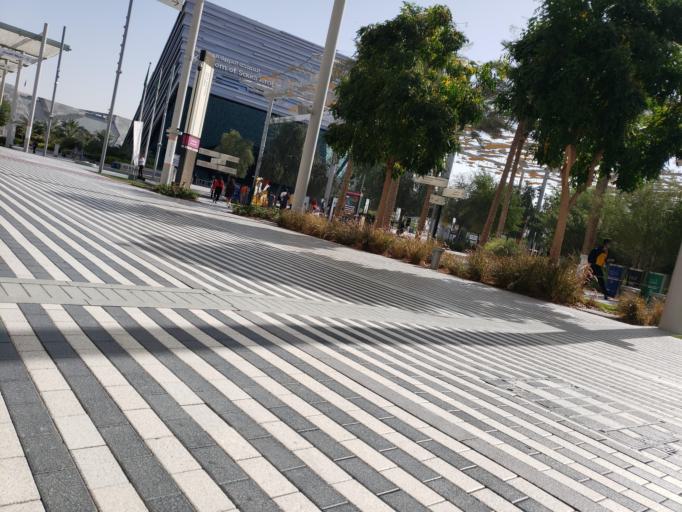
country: AE
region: Dubai
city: Dubai
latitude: 24.9626
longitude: 55.1521
